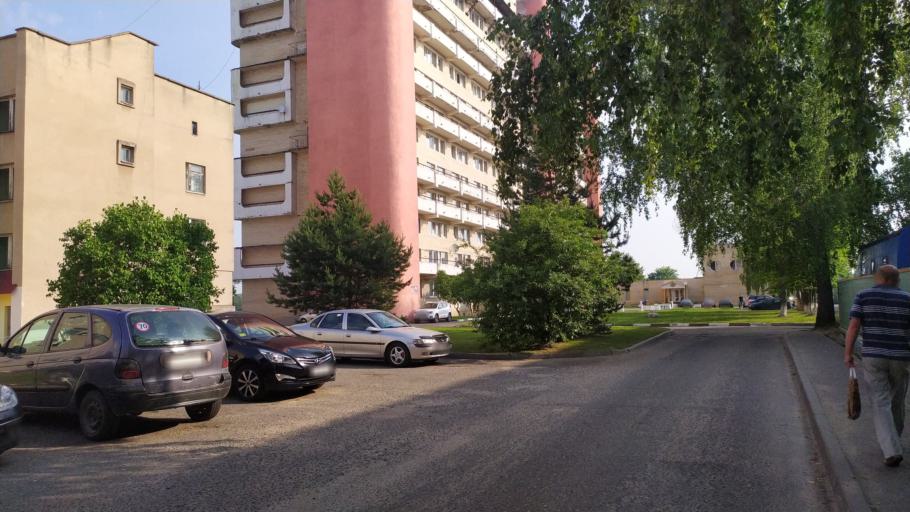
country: BY
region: Vitebsk
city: Navapolatsk
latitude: 55.5354
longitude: 28.6493
